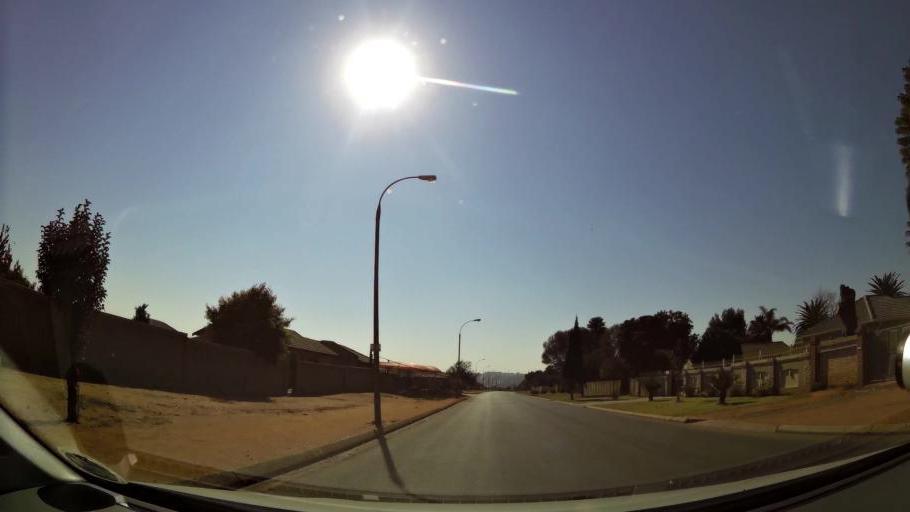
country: ZA
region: Gauteng
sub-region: Ekurhuleni Metropolitan Municipality
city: Tembisa
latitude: -26.0426
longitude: 28.2057
